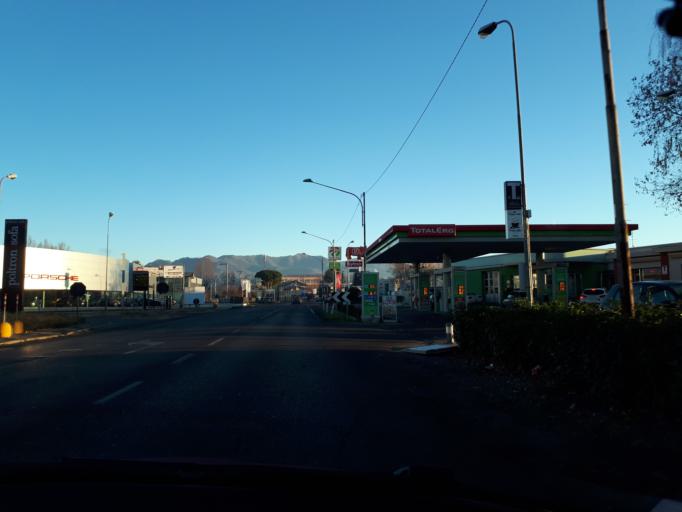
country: IT
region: Lombardy
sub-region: Provincia di Como
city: Grandate
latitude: 45.7623
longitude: 9.0547
